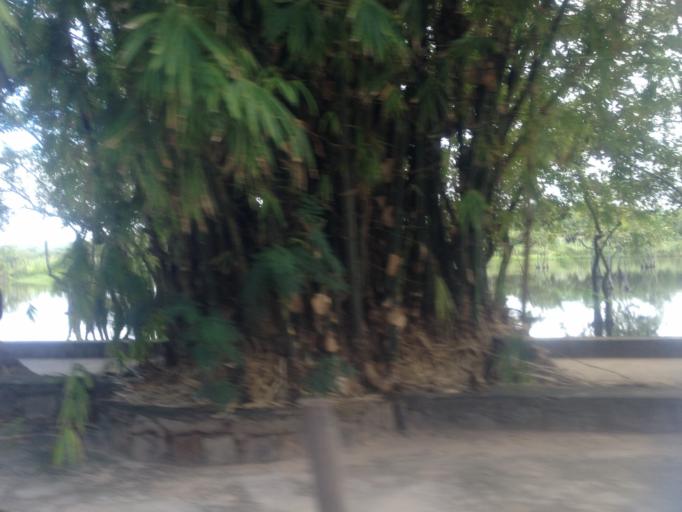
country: BR
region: Bahia
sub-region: Mata De Sao Joao
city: Mata de Sao Joao
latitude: -12.5758
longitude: -38.0084
